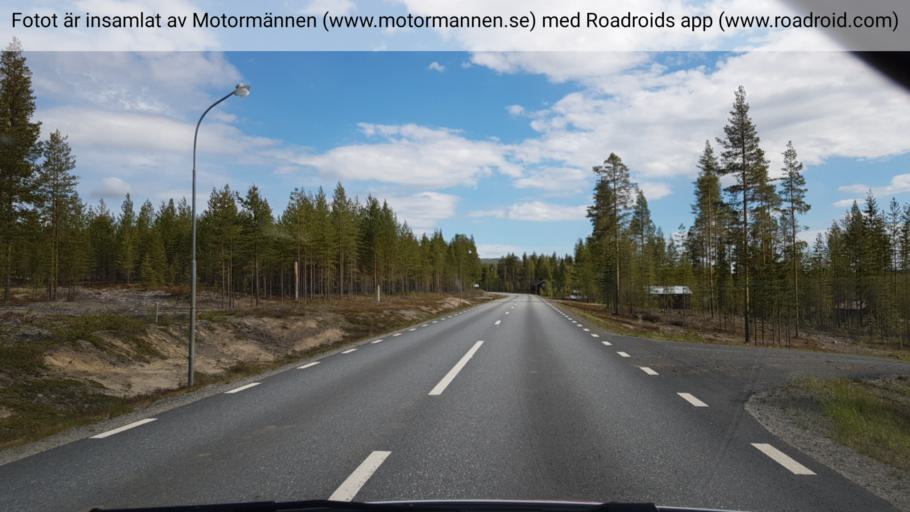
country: SE
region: Vaesterbotten
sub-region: Bjurholms Kommun
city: Bjurholm
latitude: 64.2854
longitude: 19.2110
